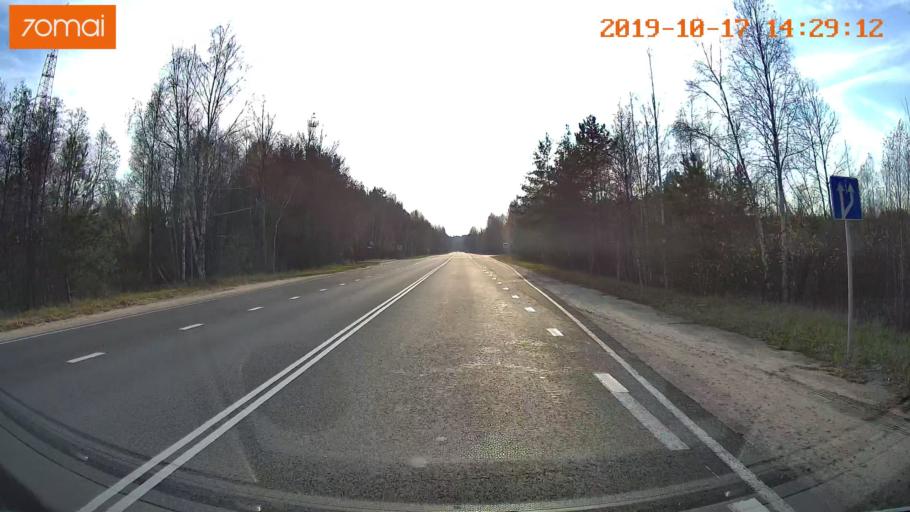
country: RU
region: Rjazan
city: Solotcha
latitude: 54.9637
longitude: 39.9446
